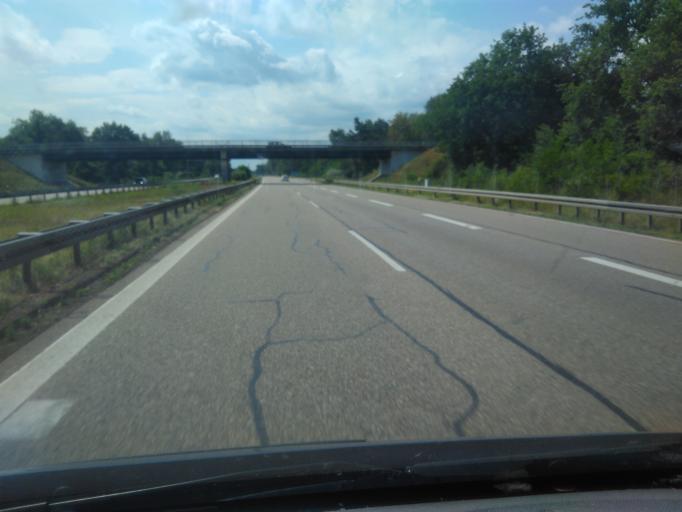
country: DE
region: Baden-Wuerttemberg
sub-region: Freiburg Region
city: Hartheim
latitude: 47.9094
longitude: 7.5894
